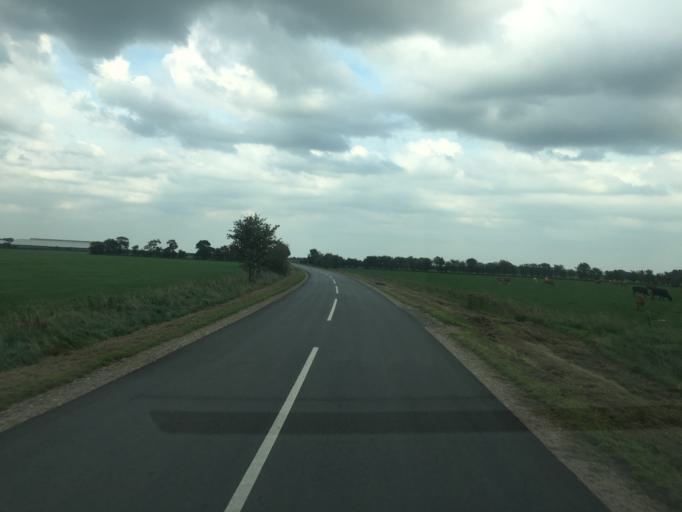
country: DK
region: South Denmark
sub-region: Tonder Kommune
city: Logumkloster
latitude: 55.0611
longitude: 9.0508
